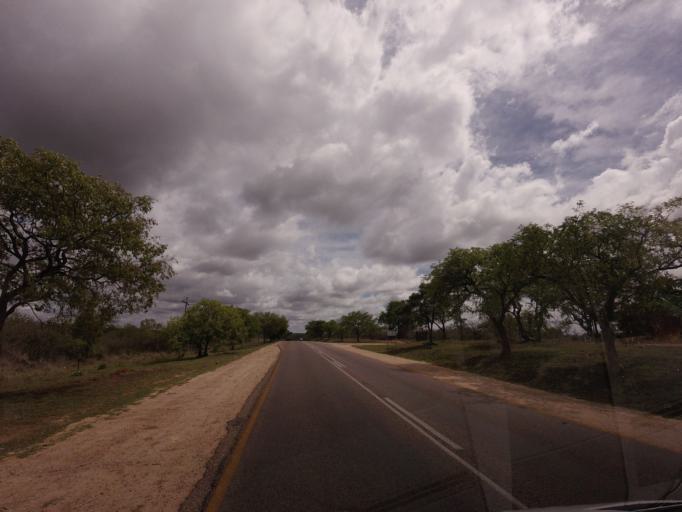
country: ZA
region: Limpopo
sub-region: Mopani District Municipality
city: Hoedspruit
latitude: -24.5511
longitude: 31.0386
